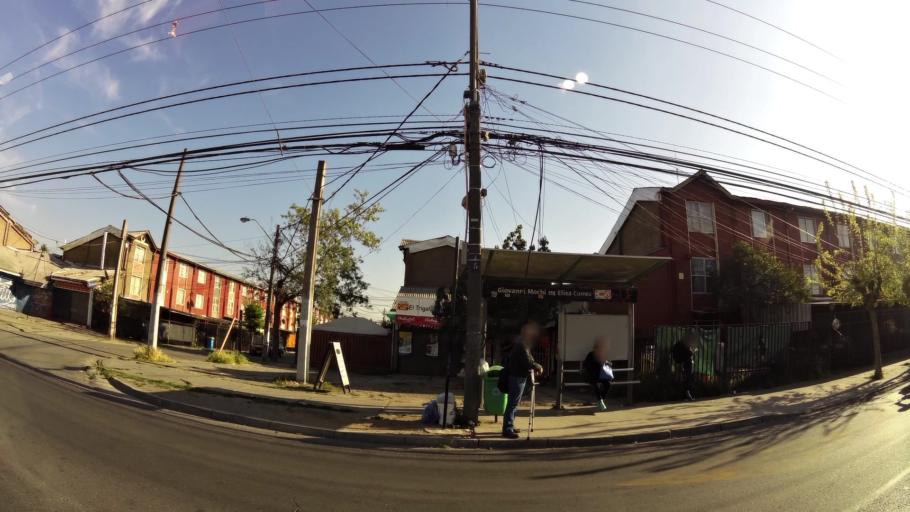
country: CL
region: Santiago Metropolitan
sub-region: Provincia de Cordillera
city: Puente Alto
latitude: -33.5691
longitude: -70.5863
